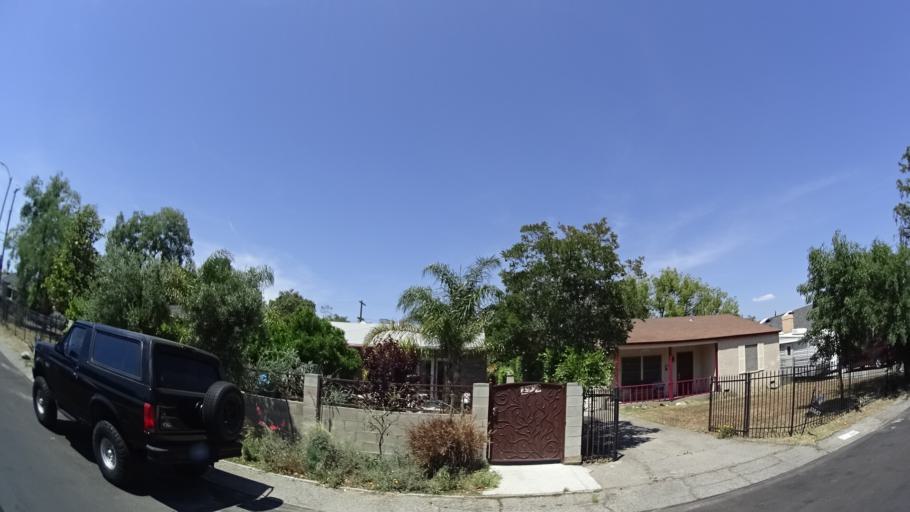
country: US
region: California
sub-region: Los Angeles County
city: North Hollywood
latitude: 34.1821
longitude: -118.3810
